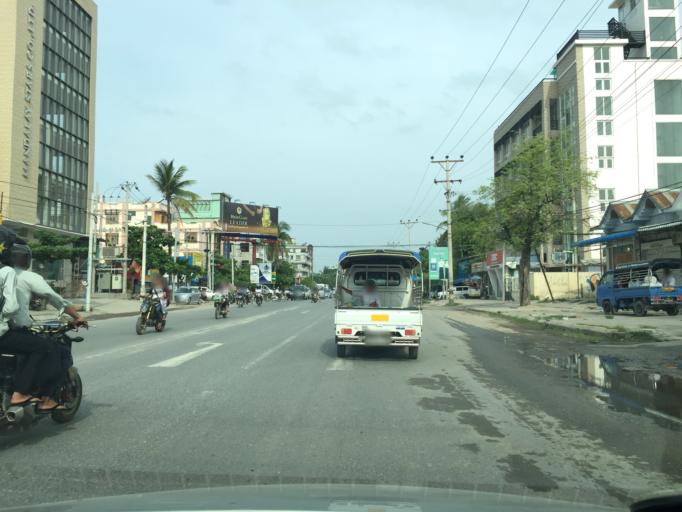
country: MM
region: Mandalay
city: Mandalay
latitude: 21.9681
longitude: 96.1020
